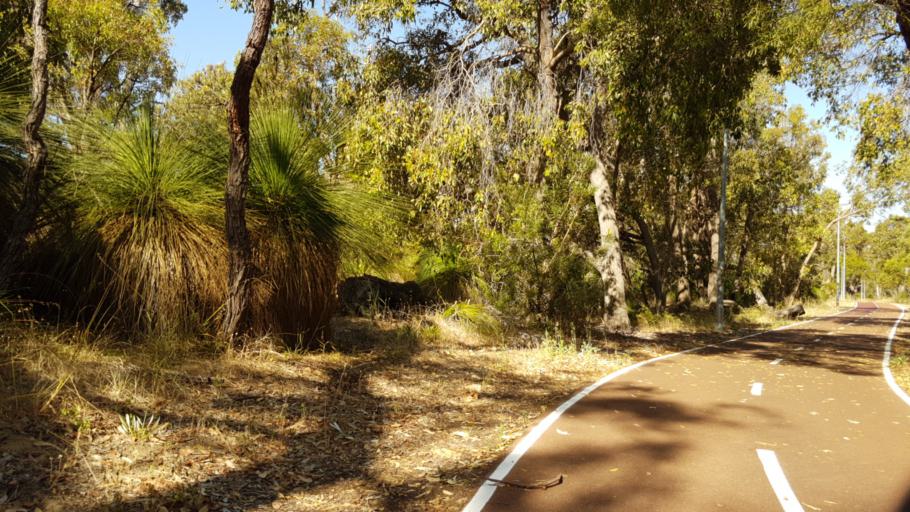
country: AU
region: Western Australia
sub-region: Stirling
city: Stirling
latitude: -31.8556
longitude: 115.8025
